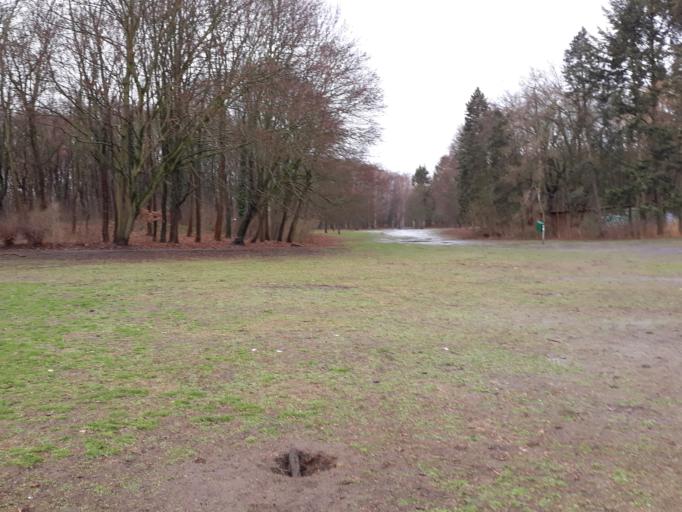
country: DE
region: Berlin
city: Reinickendorf
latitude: 52.5484
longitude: 13.3297
